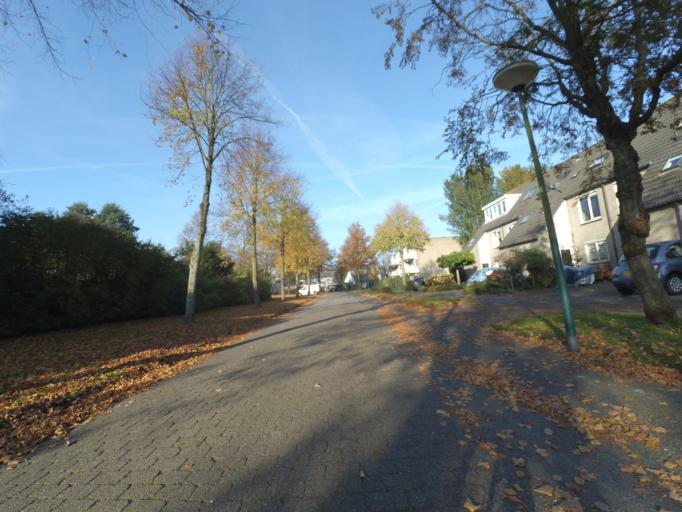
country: NL
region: Utrecht
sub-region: Gemeente Leusden
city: Leusden
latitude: 52.1396
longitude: 5.4334
